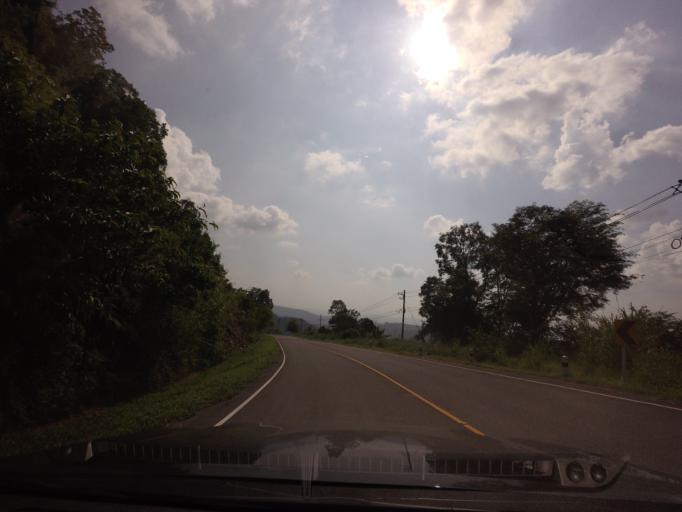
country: TH
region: Nan
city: Santi Suk
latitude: 18.9807
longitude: 100.9941
